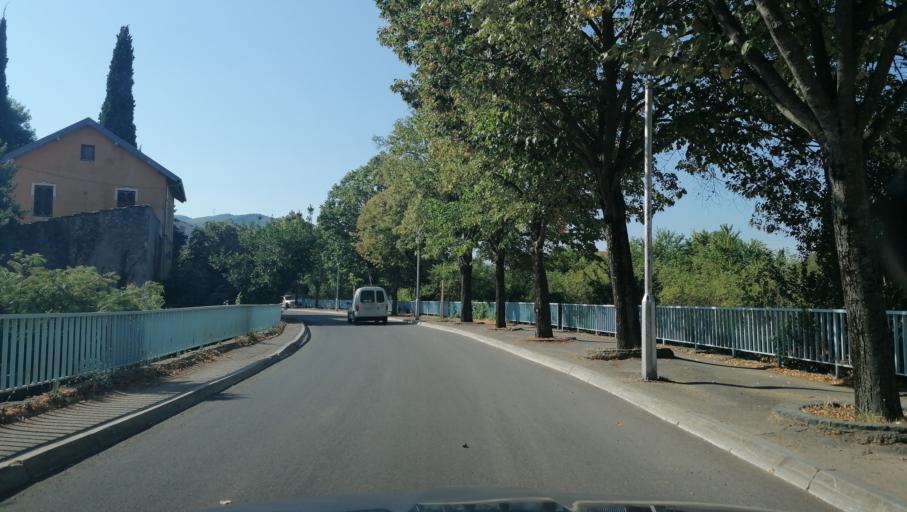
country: BA
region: Republika Srpska
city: Trebinje
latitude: 42.7134
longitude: 18.3488
